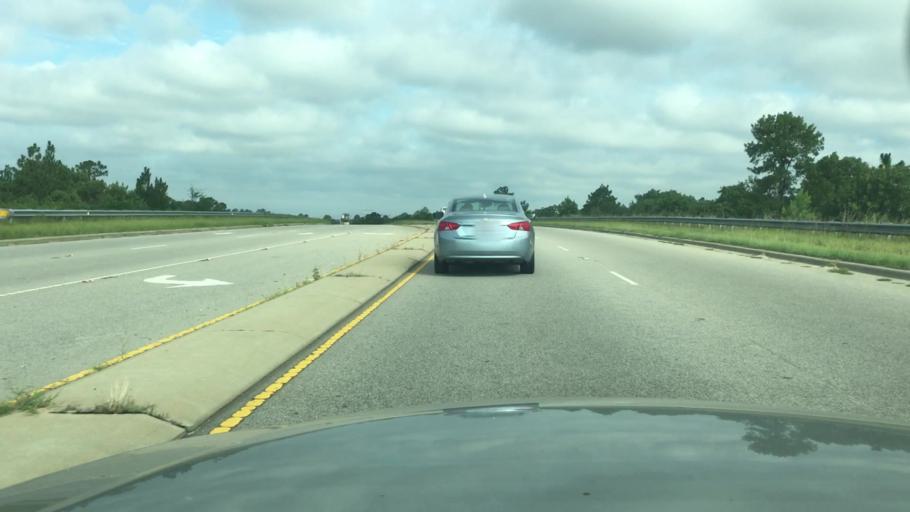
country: US
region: North Carolina
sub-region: Cumberland County
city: Hope Mills
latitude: 34.9892
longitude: -78.9374
